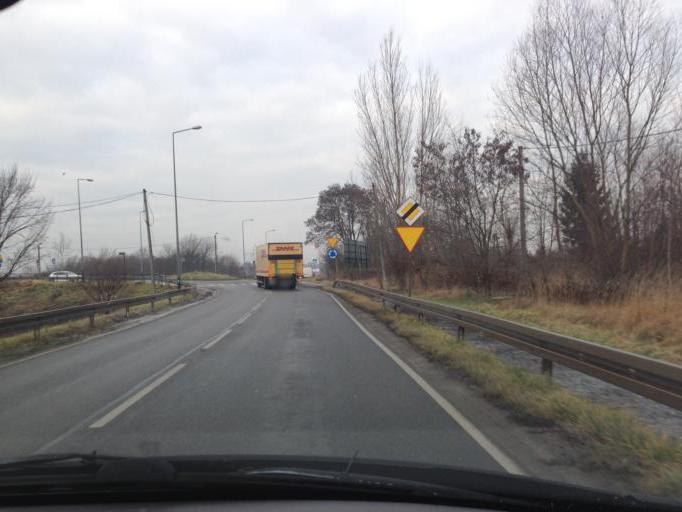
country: PL
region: Lesser Poland Voivodeship
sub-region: Powiat wielicki
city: Kokotow
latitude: 50.0536
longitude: 20.0511
